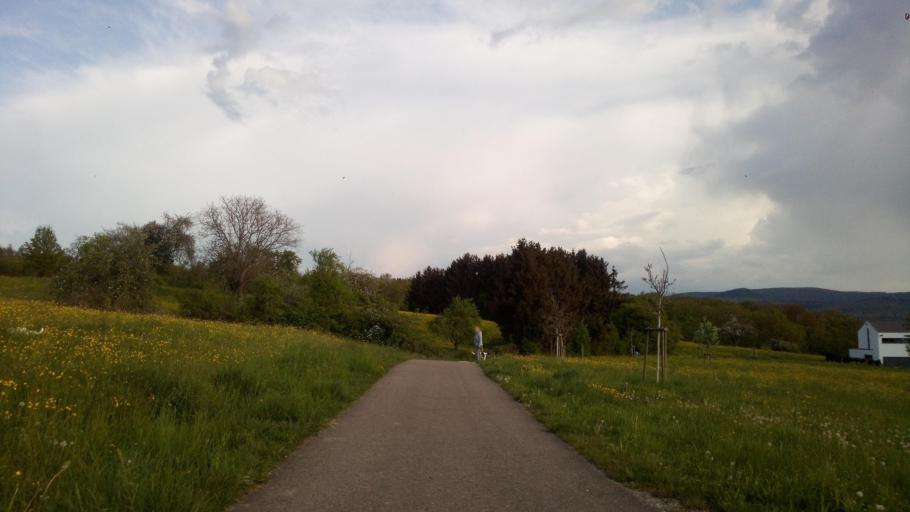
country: DE
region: Baden-Wuerttemberg
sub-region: Regierungsbezirk Stuttgart
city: Salach
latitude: 48.6989
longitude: 9.7512
